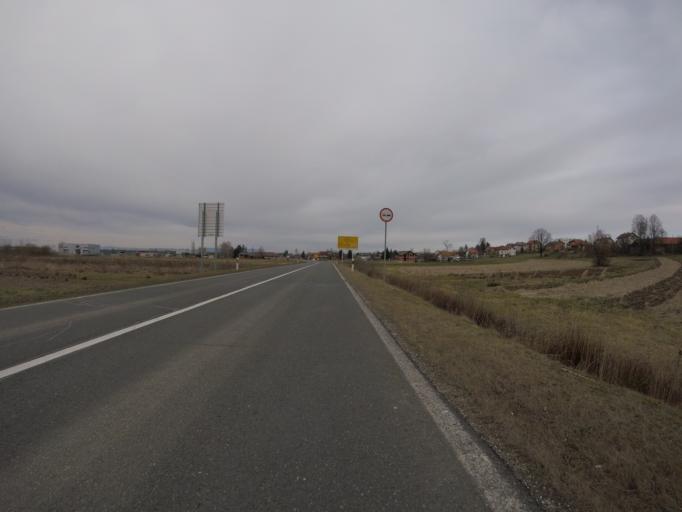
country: HR
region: Grad Zagreb
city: Horvati
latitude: 45.5822
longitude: 15.8585
